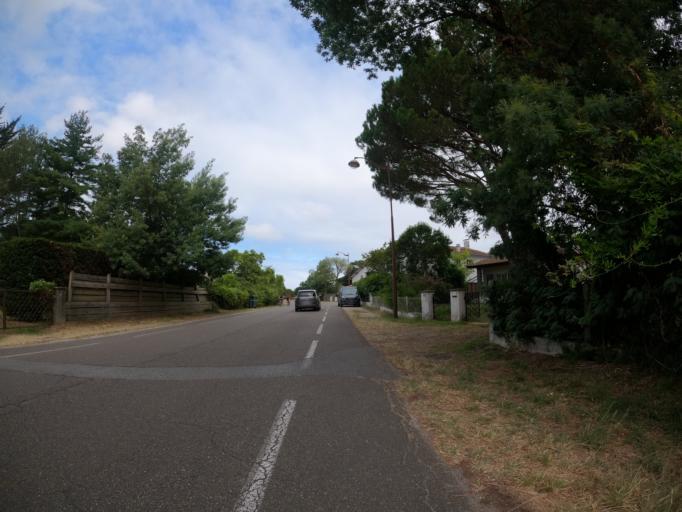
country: FR
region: Aquitaine
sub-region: Departement des Landes
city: Leon
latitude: 43.8797
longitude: -1.3042
